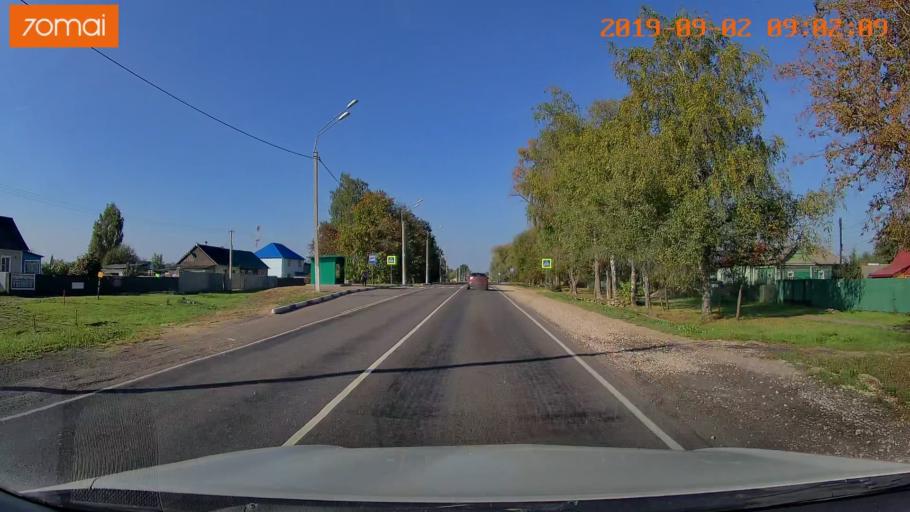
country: RU
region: Kaluga
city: Myatlevo
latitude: 54.9023
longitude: 35.6768
